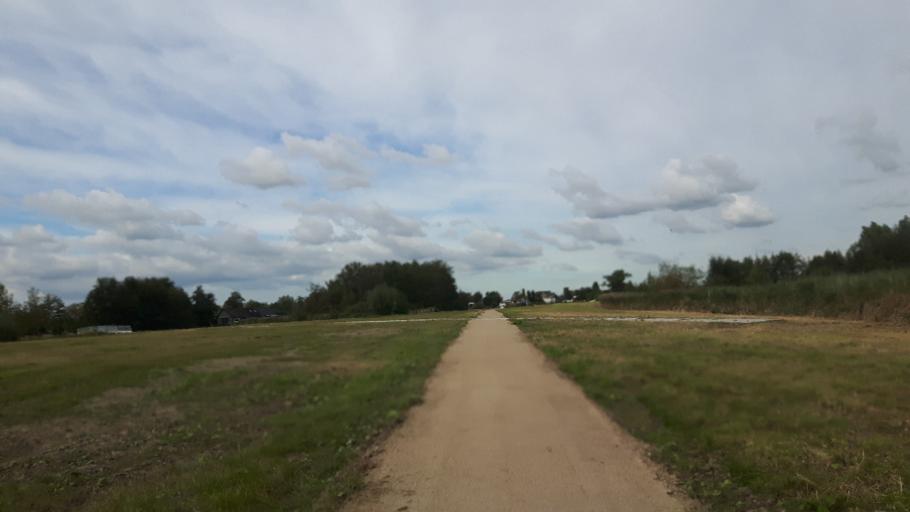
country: NL
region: South Holland
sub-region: Gemeente Nieuwkoop
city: Nieuwkoop
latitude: 52.1336
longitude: 4.7725
